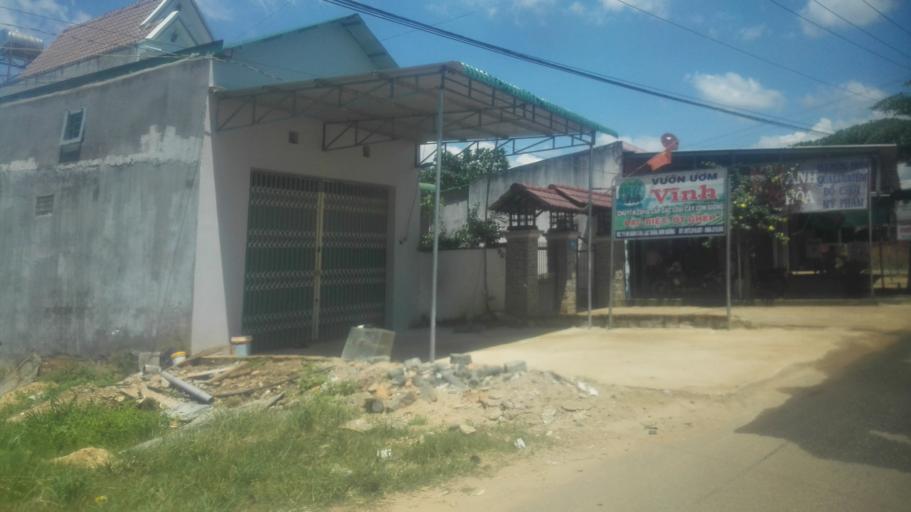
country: VN
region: Lam Dong
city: Da Lat
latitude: 11.8808
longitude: 108.3419
